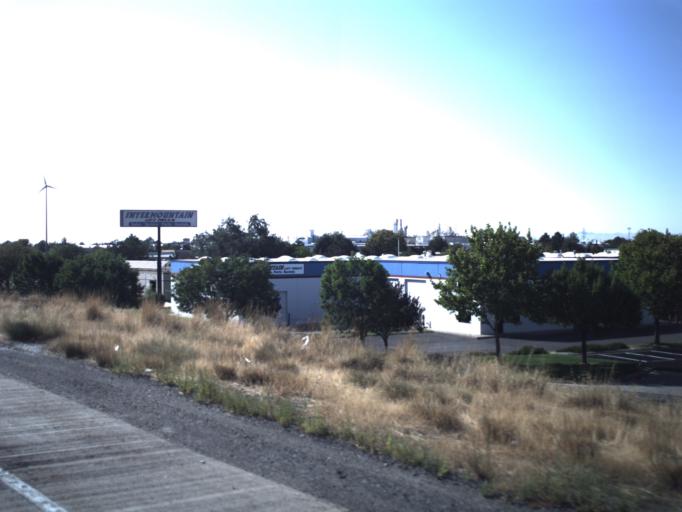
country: US
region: Utah
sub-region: Salt Lake County
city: West Valley City
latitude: 40.7270
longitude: -111.9704
